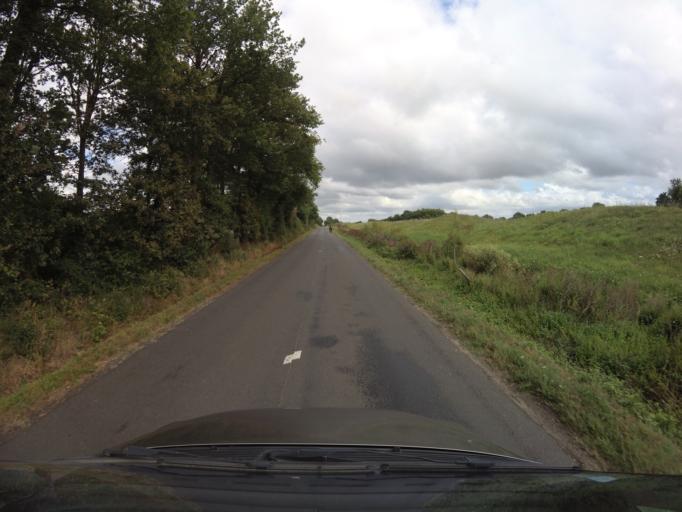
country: FR
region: Pays de la Loire
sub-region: Departement de la Loire-Atlantique
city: La Limouziniere
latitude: 47.0367
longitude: -1.5913
